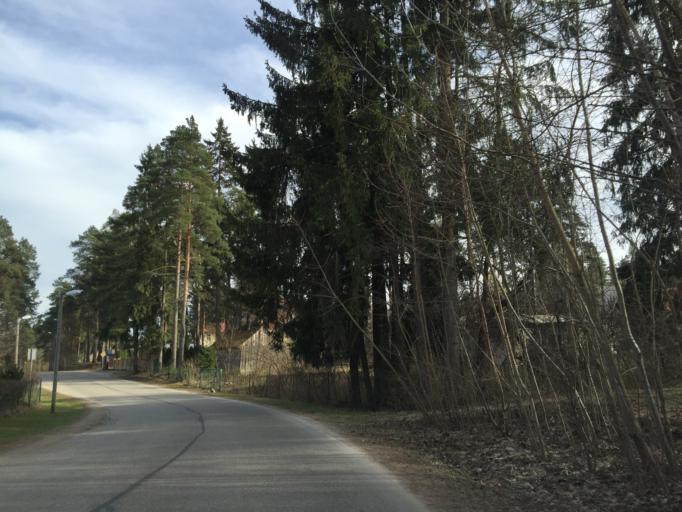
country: LV
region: Ogre
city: Ogre
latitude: 56.8114
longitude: 24.6275
